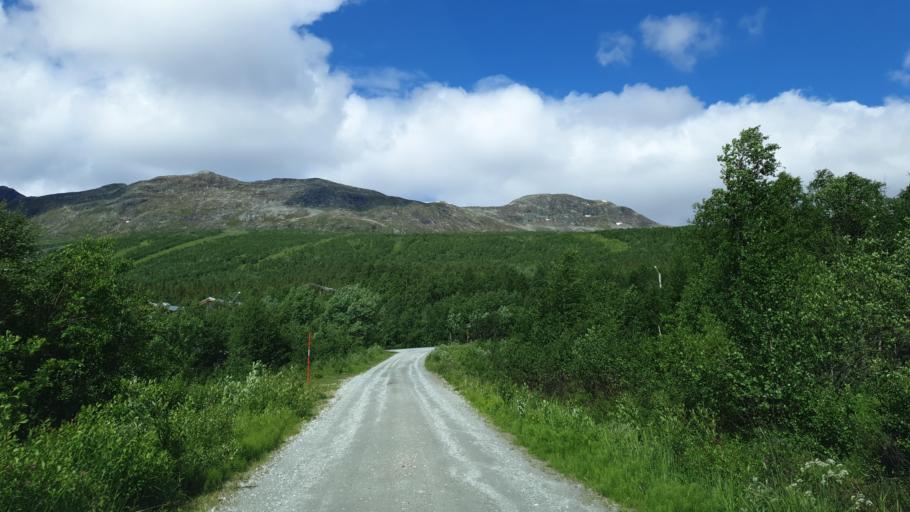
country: SE
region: Vaesterbotten
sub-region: Vilhelmina Kommun
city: Sjoberg
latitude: 65.2521
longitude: 15.5132
